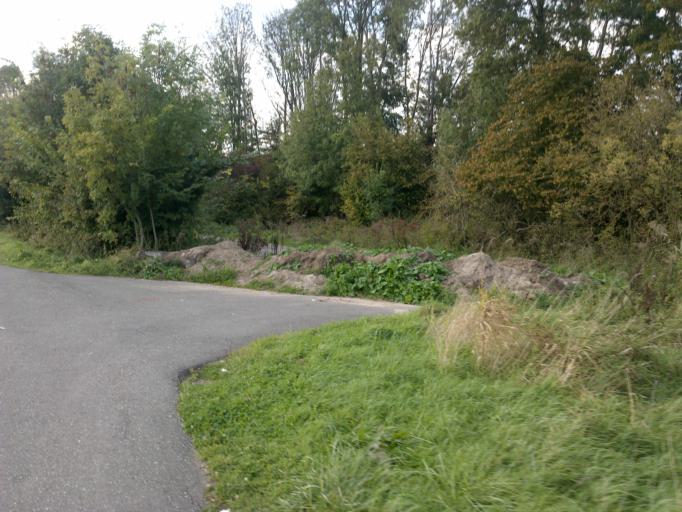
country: NL
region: South Holland
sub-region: Gemeente Sliedrecht
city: Sliedrecht
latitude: 51.7792
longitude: 4.8026
